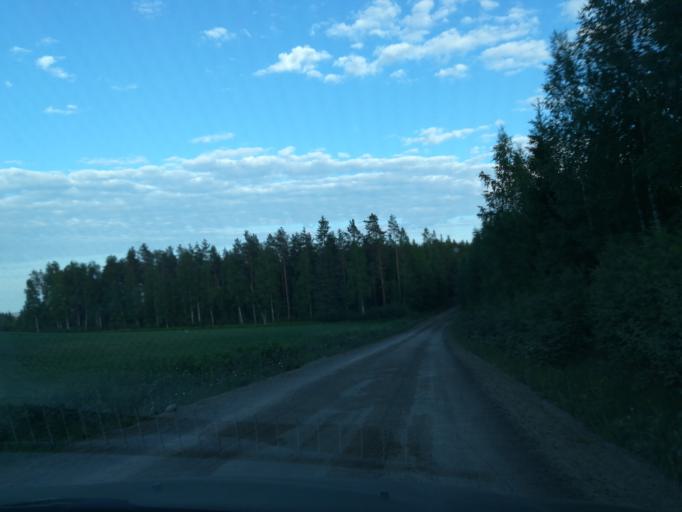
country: FI
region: Southern Savonia
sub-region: Mikkeli
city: Puumala
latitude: 61.5847
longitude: 28.1214
